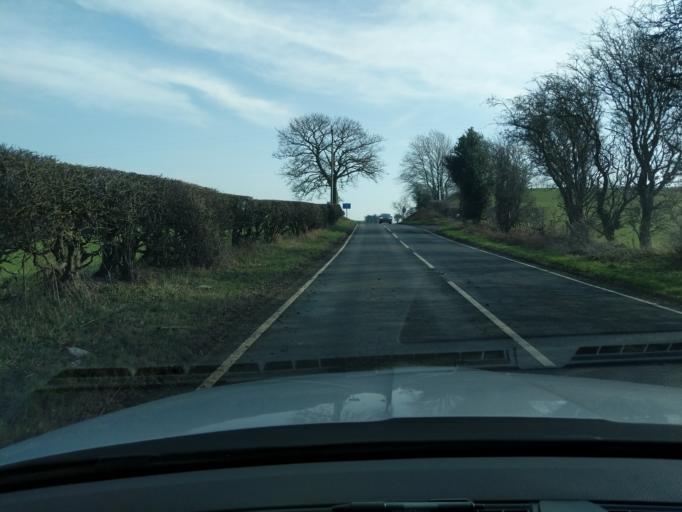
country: GB
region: England
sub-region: North Yorkshire
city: Leyburn
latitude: 54.3509
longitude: -1.8088
